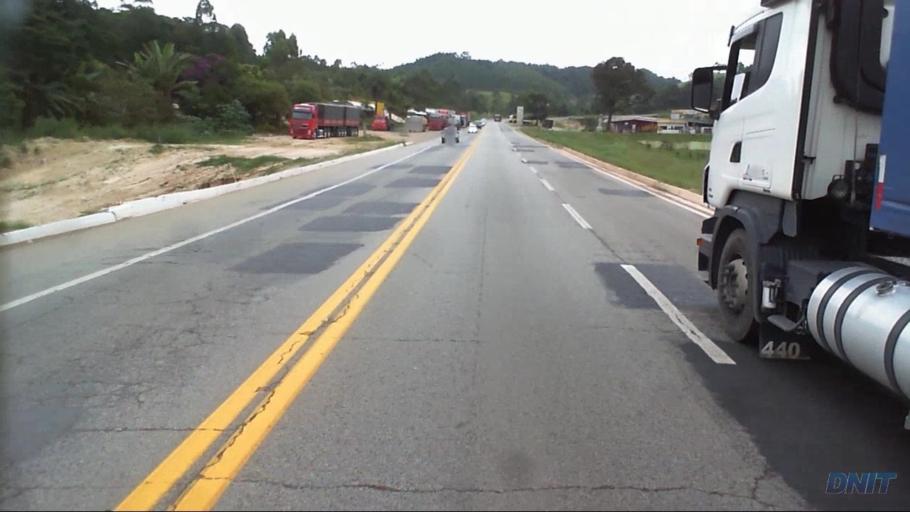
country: BR
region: Minas Gerais
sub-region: Caete
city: Caete
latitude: -19.7528
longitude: -43.5268
